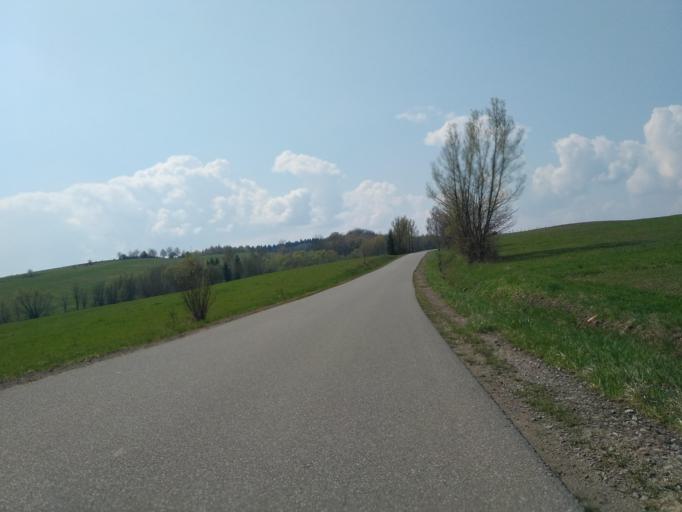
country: PL
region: Subcarpathian Voivodeship
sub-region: Powiat sanocki
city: Zarszyn
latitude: 49.5719
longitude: 22.0062
